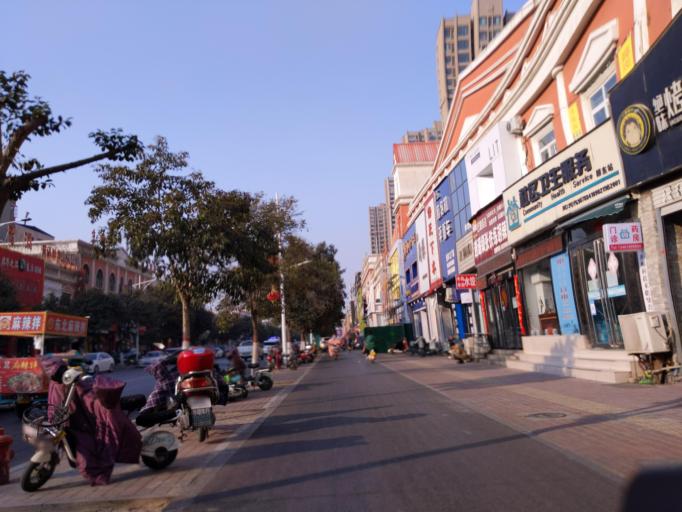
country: CN
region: Henan Sheng
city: Puyang
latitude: 35.7735
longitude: 115.0329
